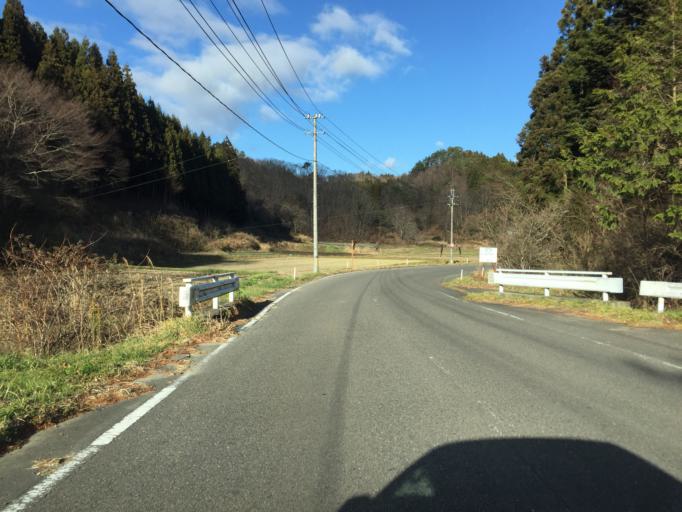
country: JP
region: Fukushima
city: Ishikawa
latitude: 37.2243
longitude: 140.6009
